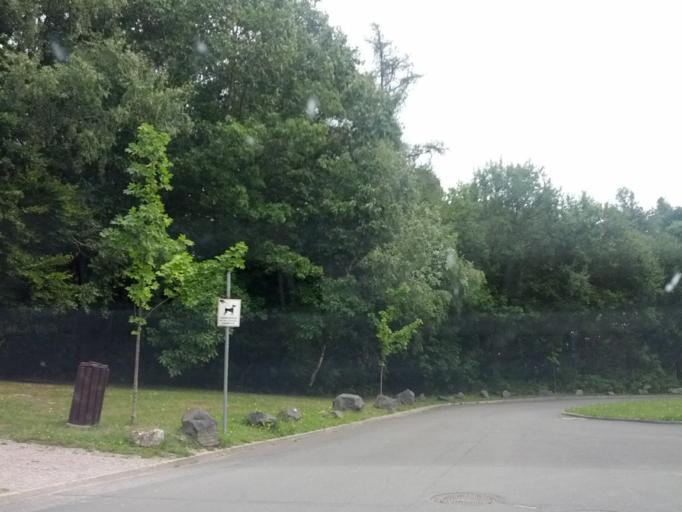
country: DE
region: Thuringia
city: Friedrichroda
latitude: 50.8654
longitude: 10.5683
